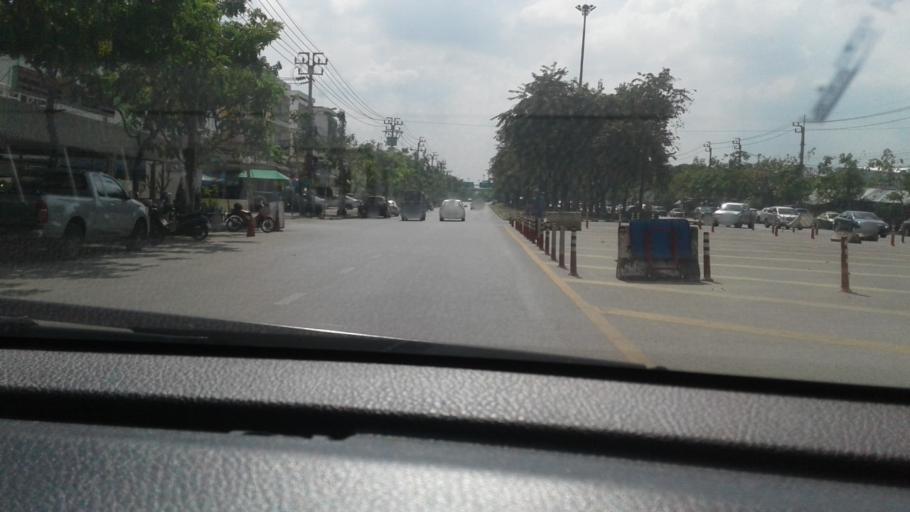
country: TH
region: Nonthaburi
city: Bang Yai
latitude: 13.7922
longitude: 100.3946
